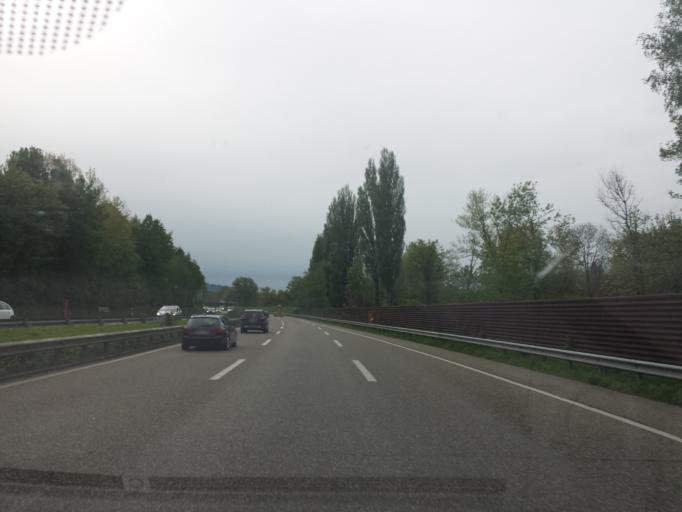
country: AT
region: Vorarlberg
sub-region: Politischer Bezirk Bregenz
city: Hochst
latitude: 47.4552
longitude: 9.6467
